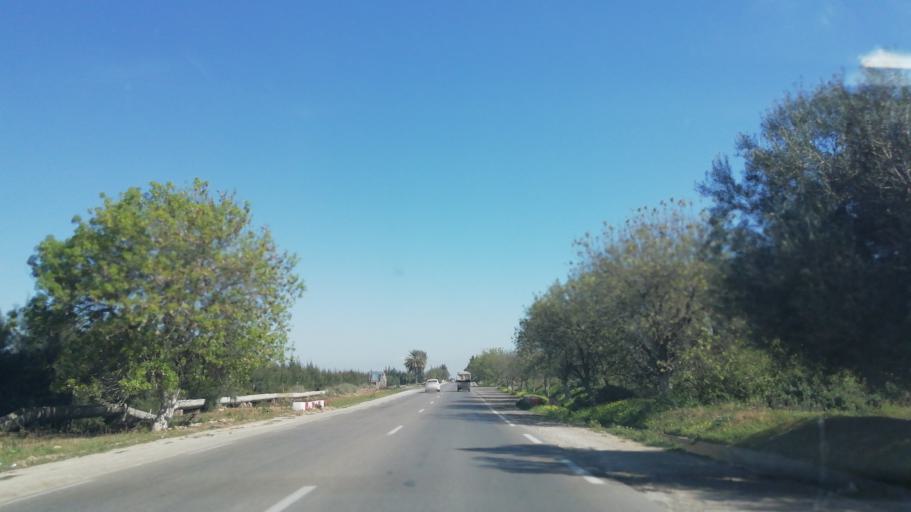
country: DZ
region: Mascara
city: Sig
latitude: 35.5461
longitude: -0.1210
